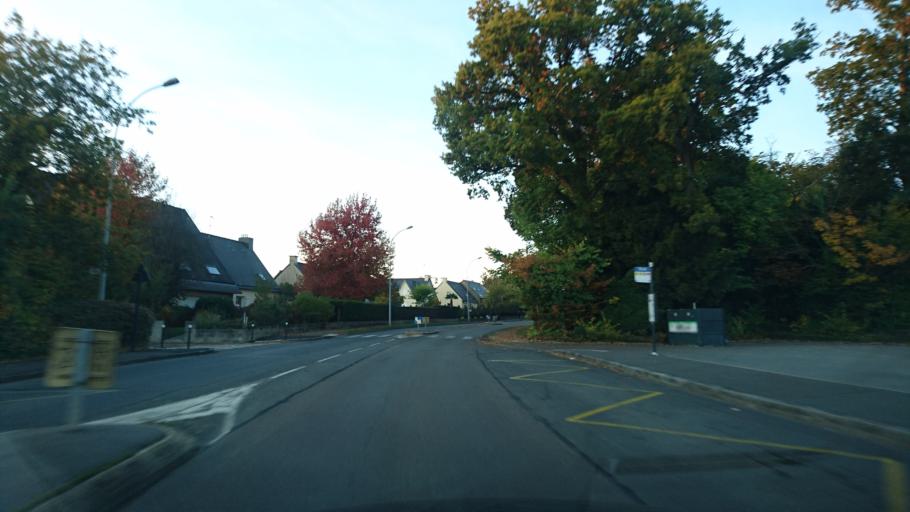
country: FR
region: Brittany
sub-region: Departement d'Ille-et-Vilaine
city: Bruz
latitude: 48.0215
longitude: -1.7522
